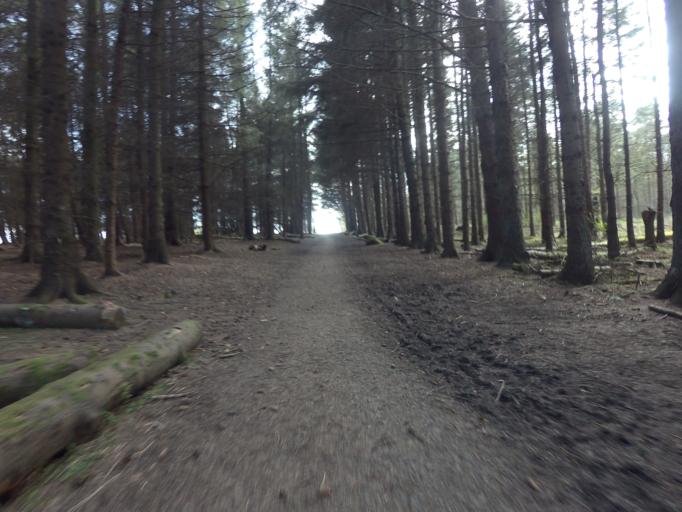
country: GB
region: Scotland
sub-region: West Lothian
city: Livingston
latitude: 55.9148
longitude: -3.5475
